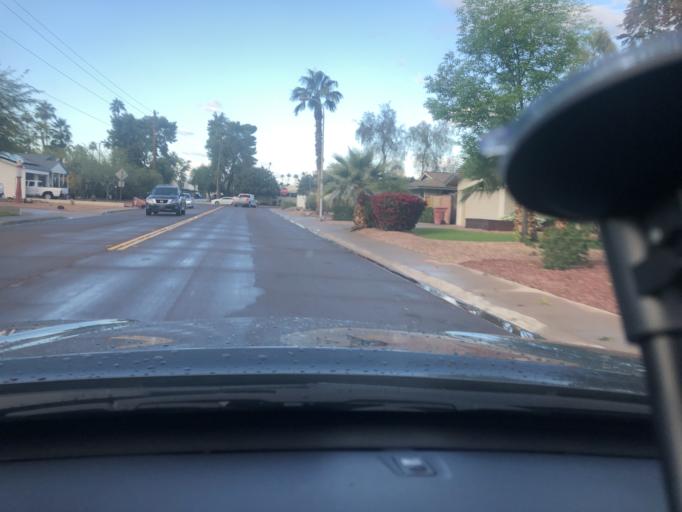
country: US
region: Arizona
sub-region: Maricopa County
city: Scottsdale
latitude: 33.4940
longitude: -111.8960
